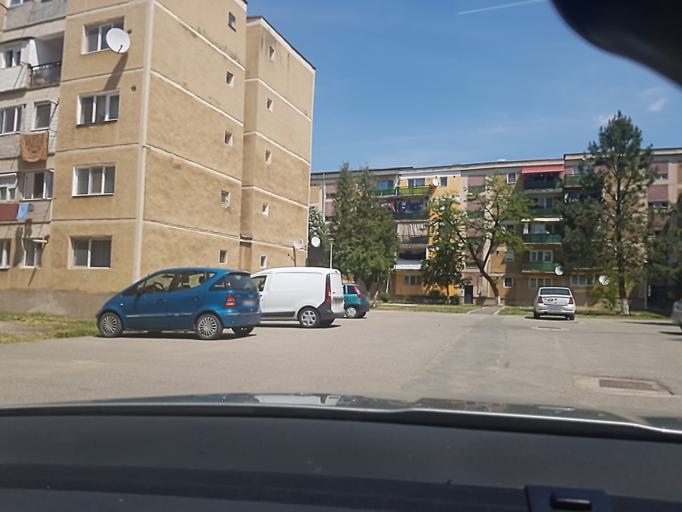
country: RO
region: Hunedoara
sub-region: Comuna Calan
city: Calan
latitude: 45.7289
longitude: 23.0283
